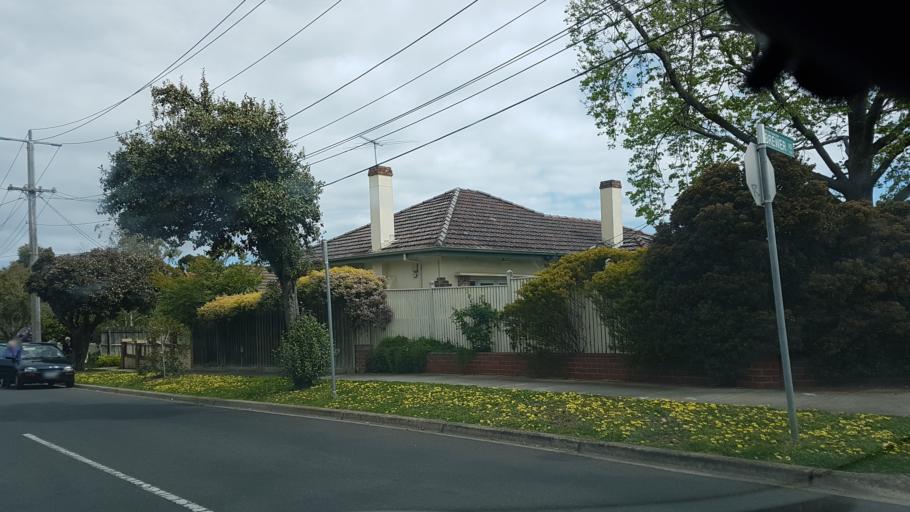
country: AU
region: Victoria
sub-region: Glen Eira
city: Bentleigh
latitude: -37.9217
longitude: 145.0329
